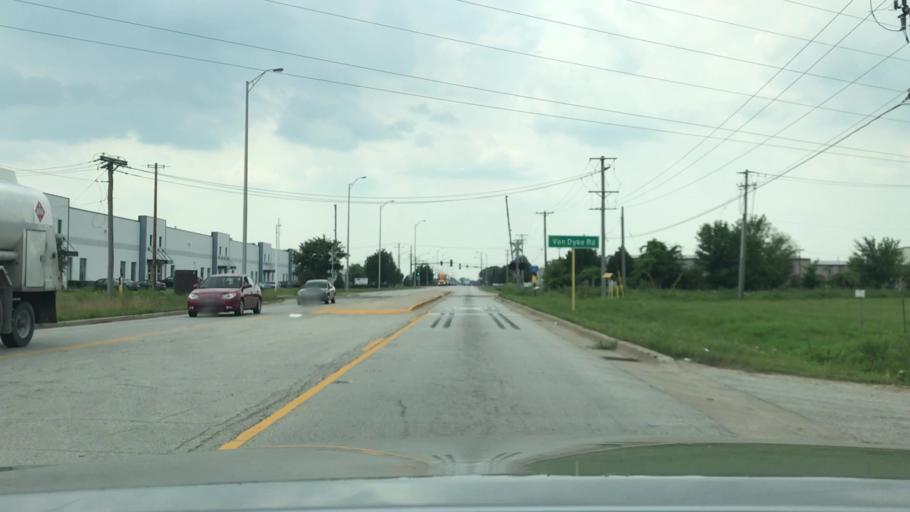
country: US
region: Illinois
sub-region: Will County
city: Plainfield
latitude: 41.6226
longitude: -88.2092
